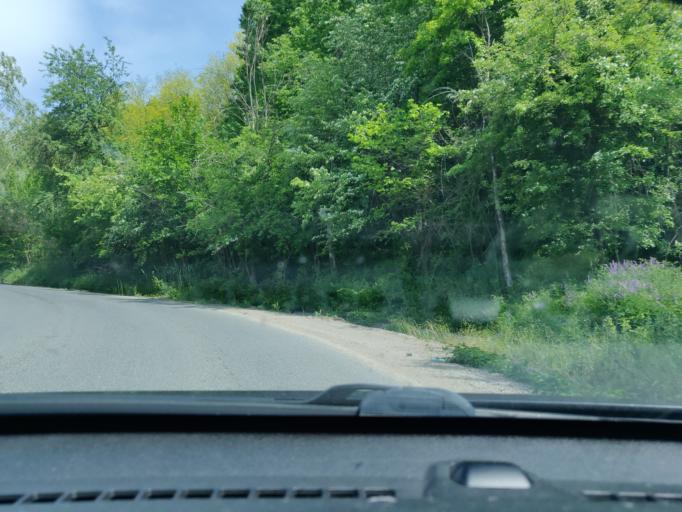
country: RO
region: Vrancea
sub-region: Comuna Vidra
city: Vidra
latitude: 45.9254
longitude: 26.8978
